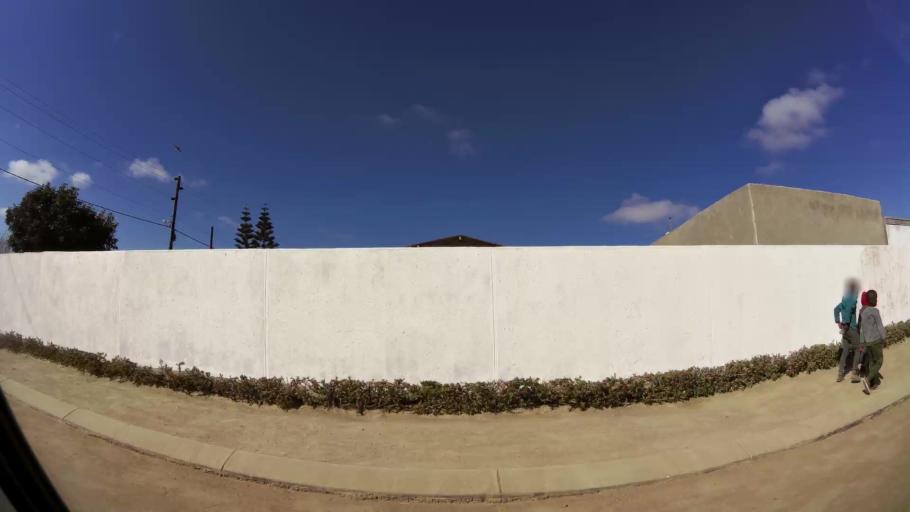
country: ZA
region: Limpopo
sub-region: Capricorn District Municipality
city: Polokwane
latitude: -23.8636
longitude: 29.3831
